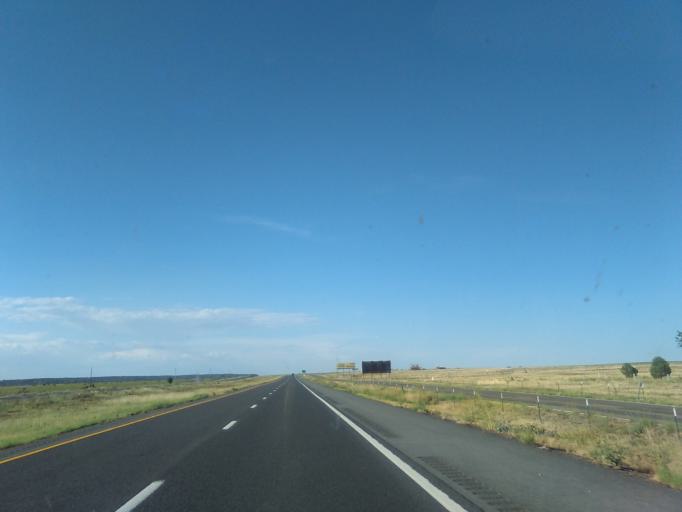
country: US
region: New Mexico
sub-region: San Miguel County
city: Las Vegas
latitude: 35.6581
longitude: -105.1882
